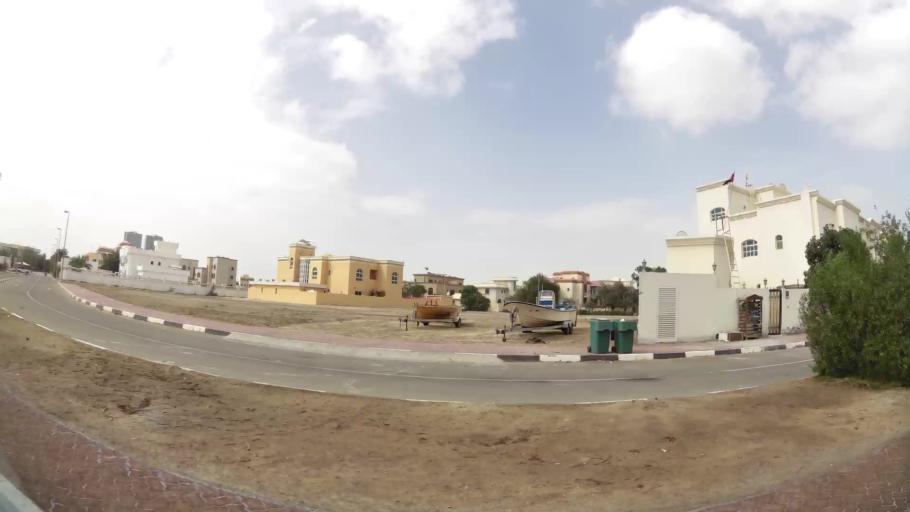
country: AE
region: Abu Dhabi
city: Abu Dhabi
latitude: 24.4025
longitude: 54.5221
